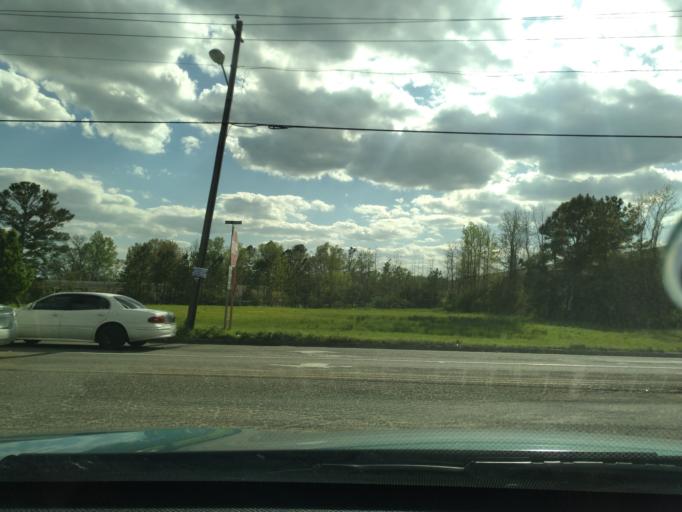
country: US
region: South Carolina
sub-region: Florence County
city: Florence
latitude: 34.2256
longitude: -79.7952
